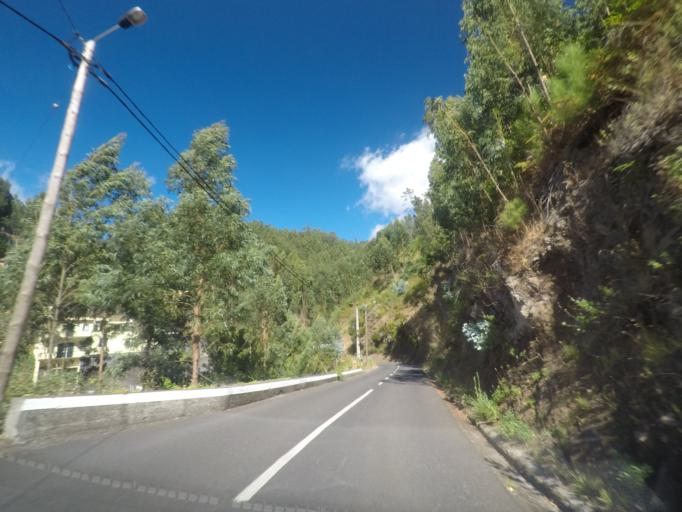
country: PT
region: Madeira
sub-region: Ribeira Brava
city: Campanario
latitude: 32.6882
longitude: -17.0284
